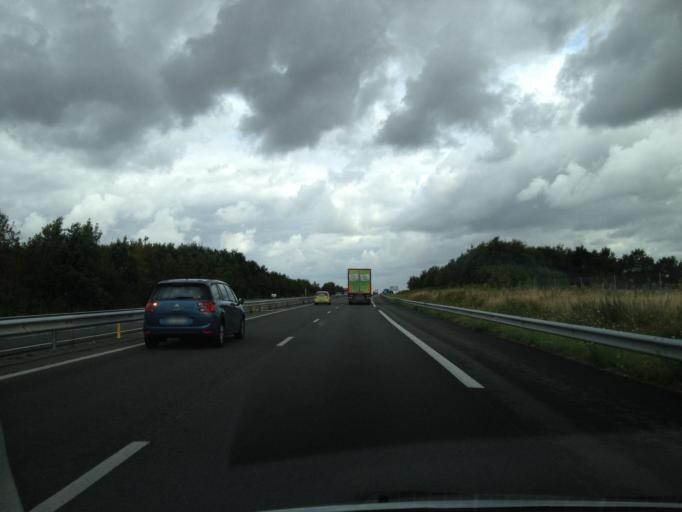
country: FR
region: Pays de la Loire
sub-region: Departement de la Vendee
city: Bournezeau
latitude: 46.6323
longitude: -1.1492
